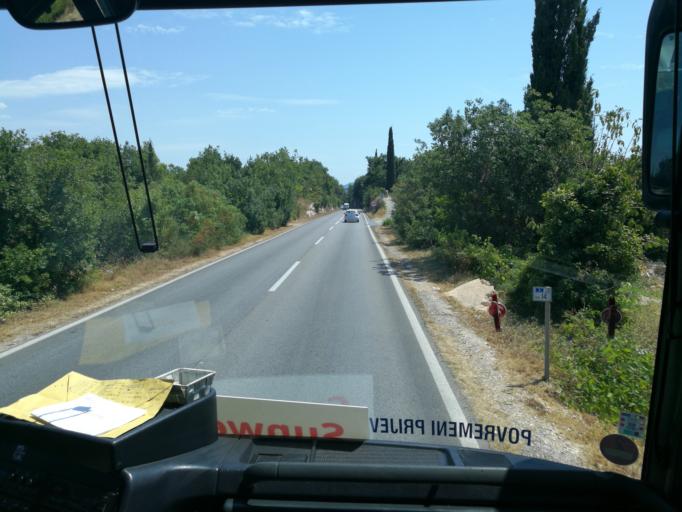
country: HR
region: Dubrovacko-Neretvanska
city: Jasenice
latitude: 42.5607
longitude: 18.2565
